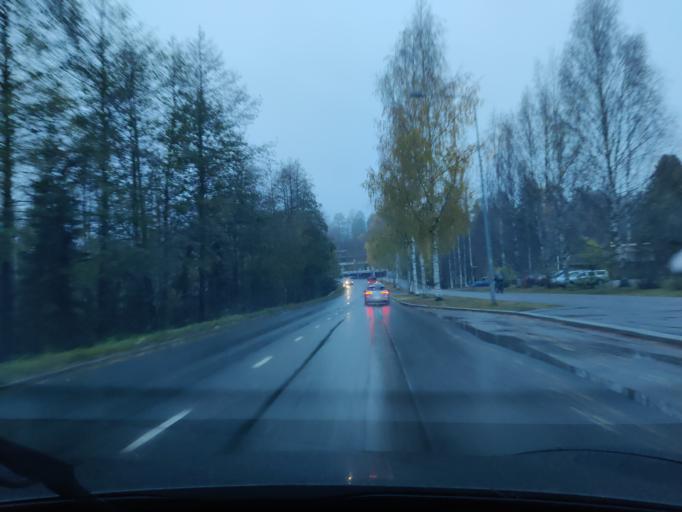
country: FI
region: Northern Savo
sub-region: Kuopio
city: Kuopio
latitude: 62.8467
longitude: 27.6491
